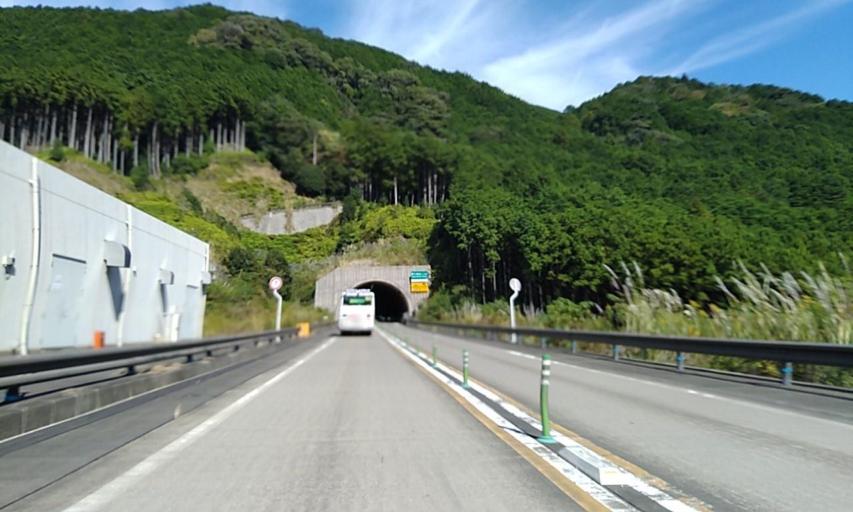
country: JP
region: Mie
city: Owase
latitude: 33.9749
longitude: 136.1657
